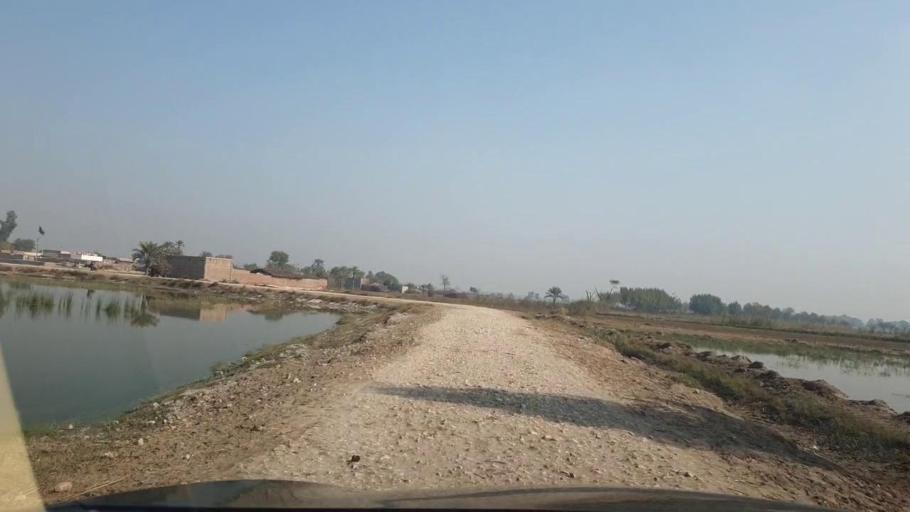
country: PK
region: Sindh
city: Ubauro
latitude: 28.1390
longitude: 69.7491
